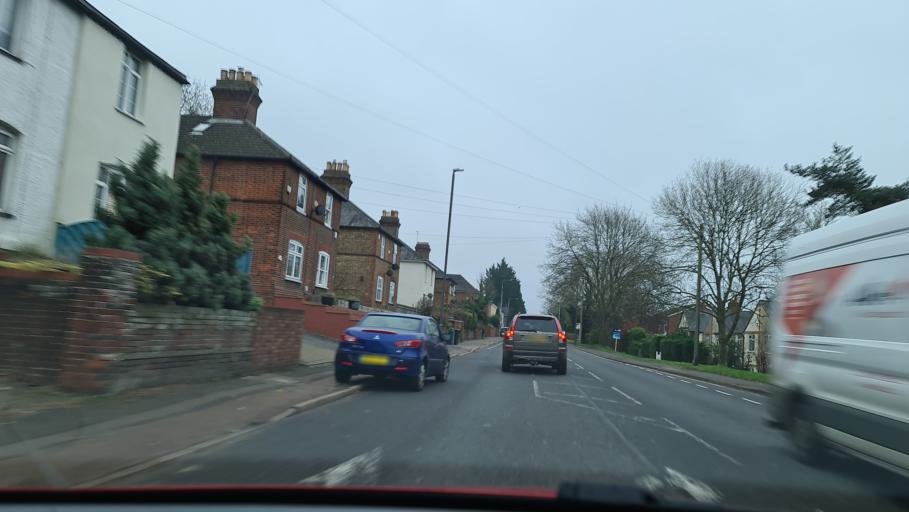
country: GB
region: England
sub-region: Buckinghamshire
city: High Wycombe
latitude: 51.6434
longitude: -0.7923
